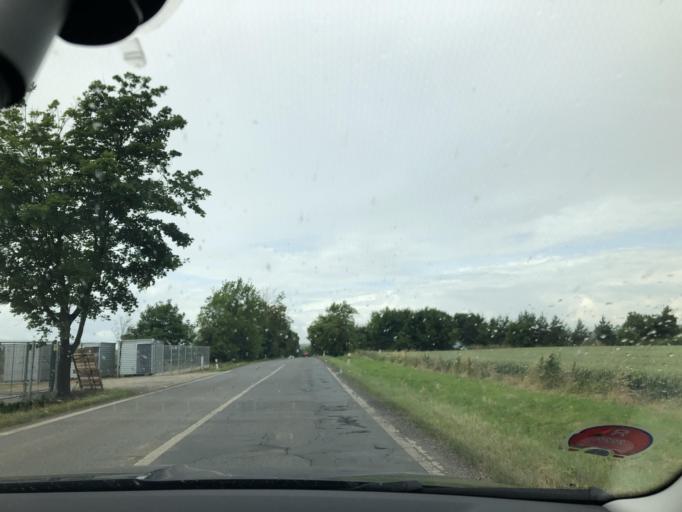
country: CZ
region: Central Bohemia
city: Horomerice
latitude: 50.1427
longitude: 14.3417
